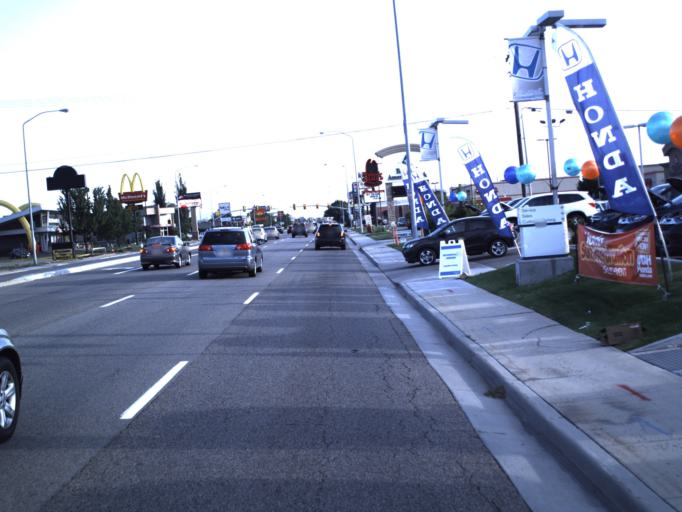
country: US
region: Utah
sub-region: Salt Lake County
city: Murray
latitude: 40.6450
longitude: -111.8890
